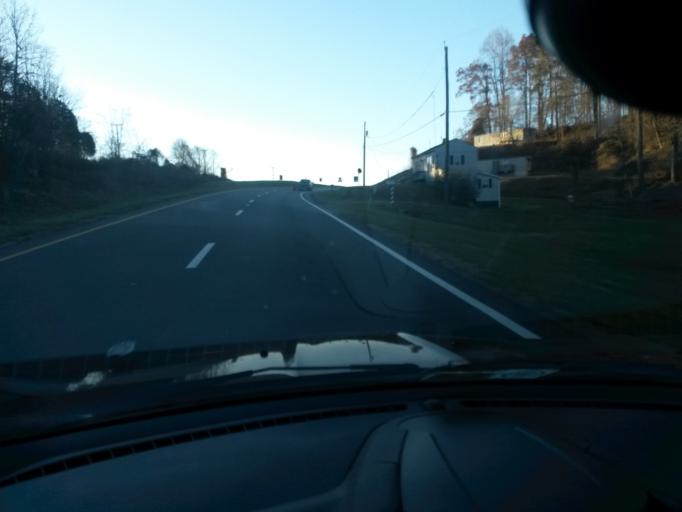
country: US
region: Virginia
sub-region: Franklin County
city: Henry Fork
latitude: 36.8941
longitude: -79.8660
